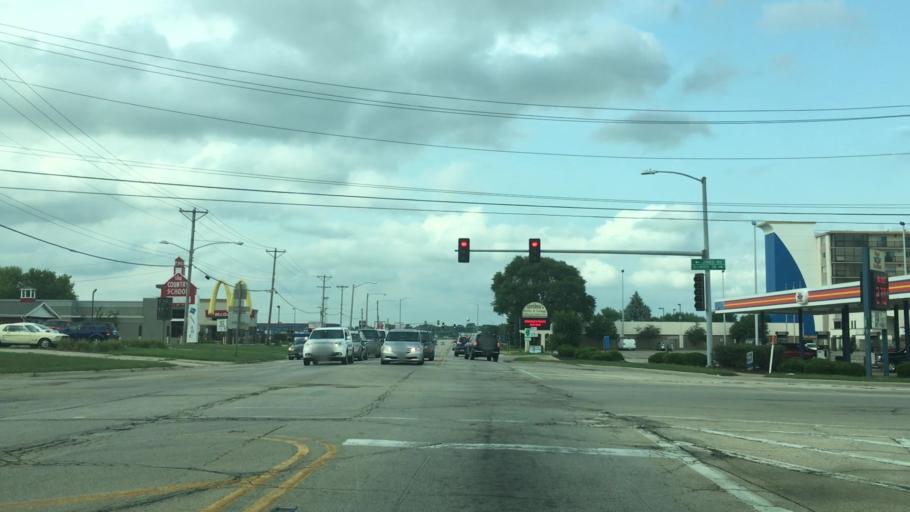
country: US
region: Illinois
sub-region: Ogle County
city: Rochelle
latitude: 41.9338
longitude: -89.0683
